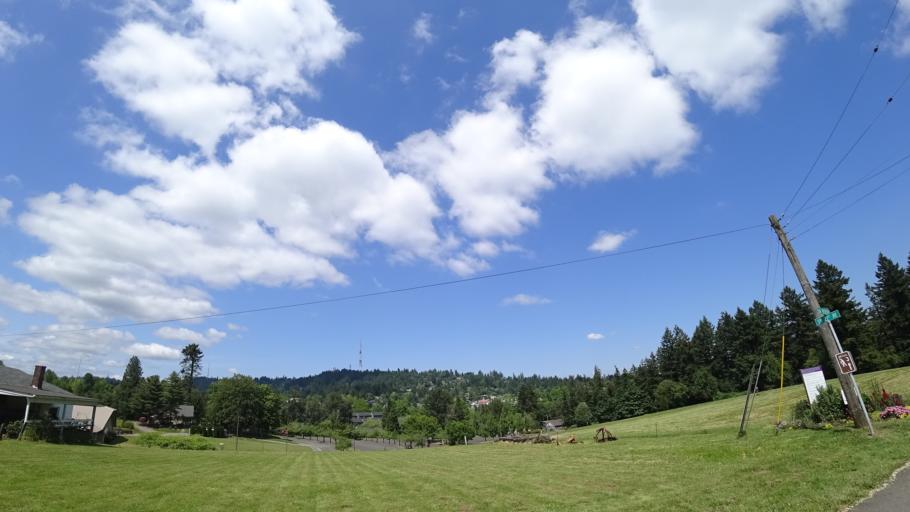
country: US
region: Oregon
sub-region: Multnomah County
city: Portland
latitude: 45.4724
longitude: -122.6992
